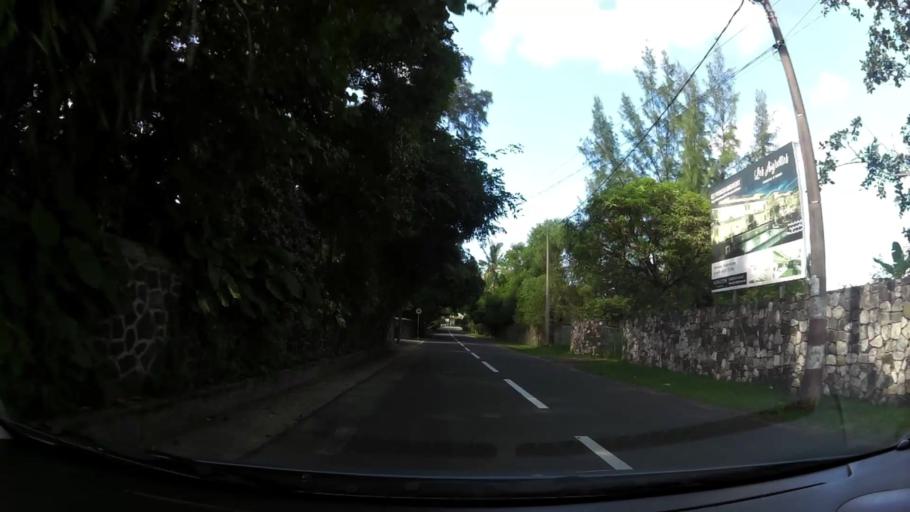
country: MU
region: Grand Port
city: Beau Vallon
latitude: -20.4257
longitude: 57.7250
